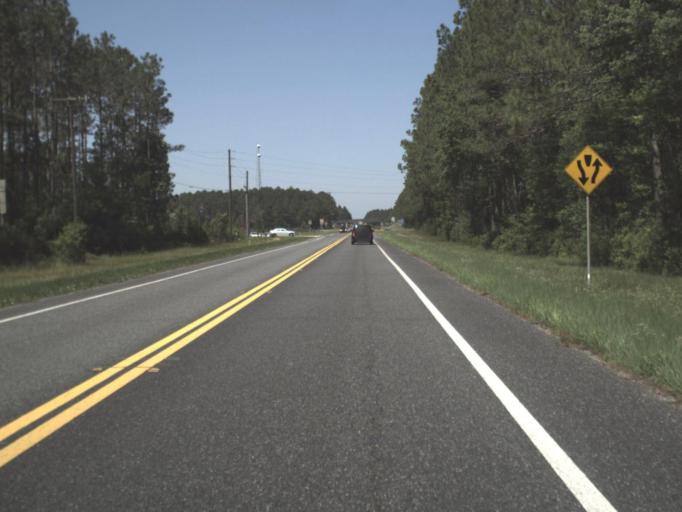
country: US
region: Florida
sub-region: Baker County
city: Macclenny
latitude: 30.2417
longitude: -82.2956
